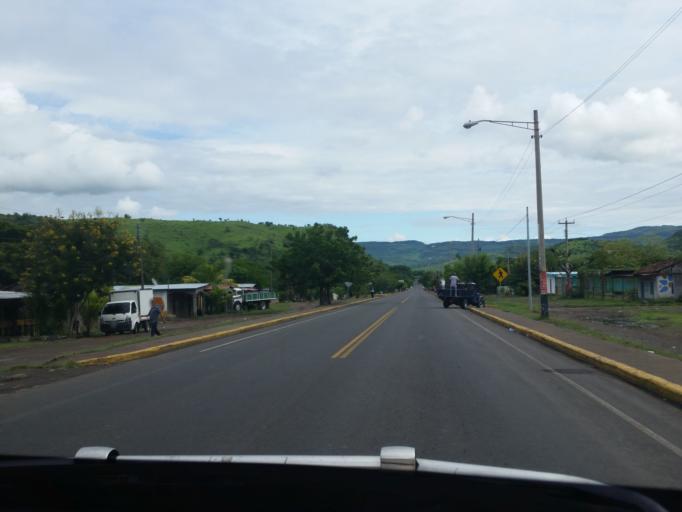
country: NI
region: Boaco
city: Teustepe
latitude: 12.4435
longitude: -86.0415
